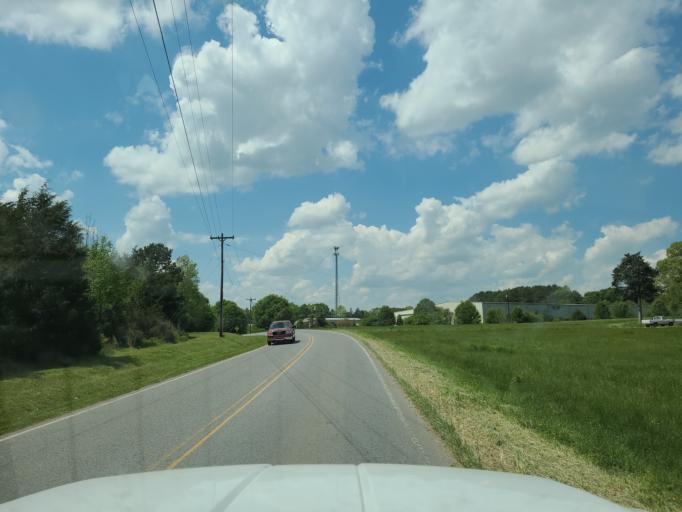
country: US
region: North Carolina
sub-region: Cleveland County
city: Shelby
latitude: 35.3247
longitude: -81.4881
